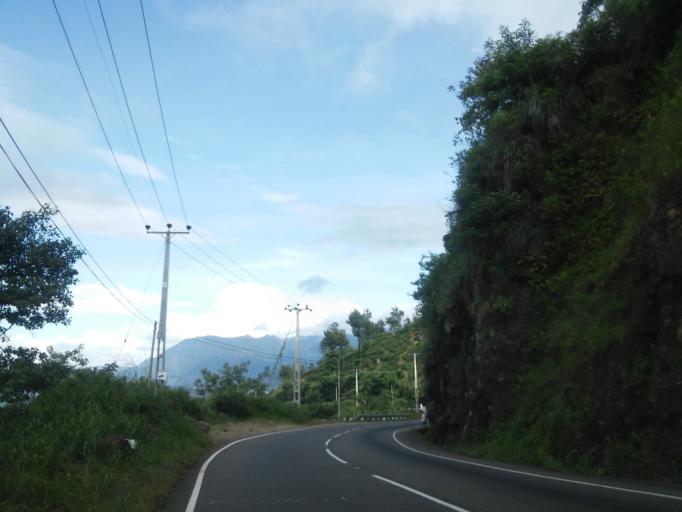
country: LK
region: Uva
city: Haputale
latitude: 6.7612
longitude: 80.9339
